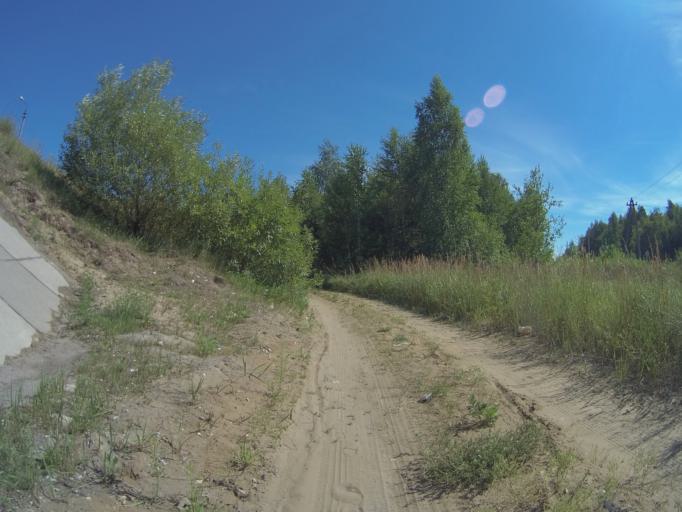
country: RU
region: Vladimir
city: Raduzhnyy
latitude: 56.0629
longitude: 40.3692
